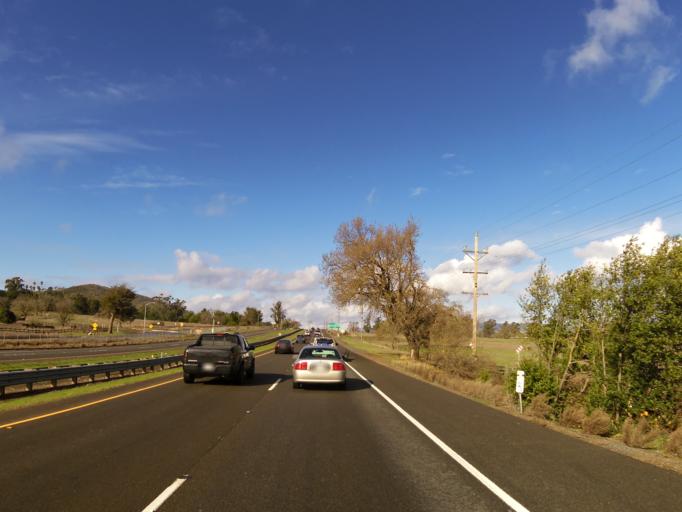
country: US
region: California
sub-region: Marin County
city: Novato
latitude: 38.1488
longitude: -122.5659
